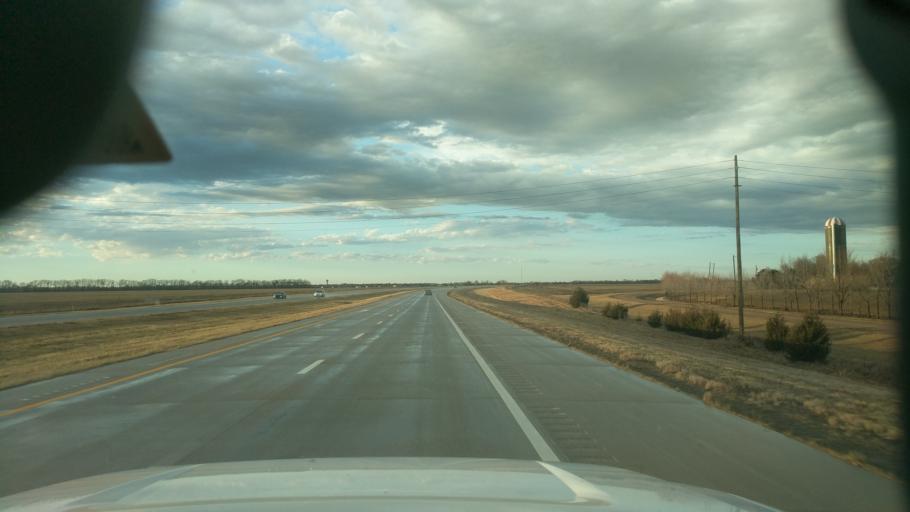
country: US
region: Kansas
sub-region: Harvey County
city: Hesston
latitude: 38.1166
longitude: -97.3892
